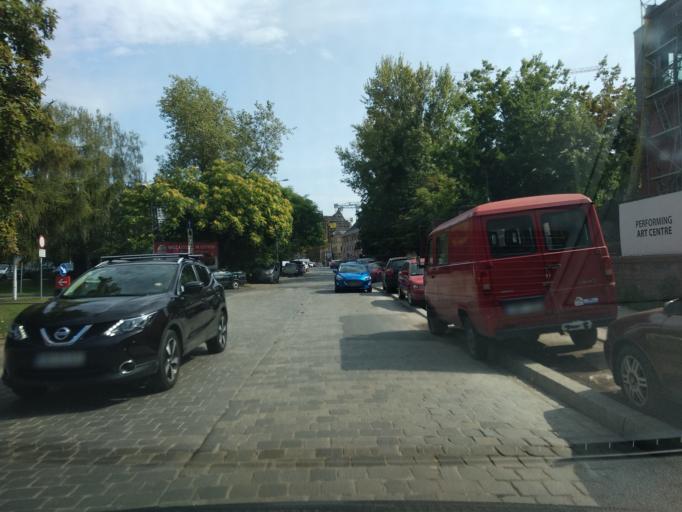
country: PL
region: Lower Silesian Voivodeship
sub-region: Powiat wroclawski
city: Wroclaw
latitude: 51.1162
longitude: 17.0229
